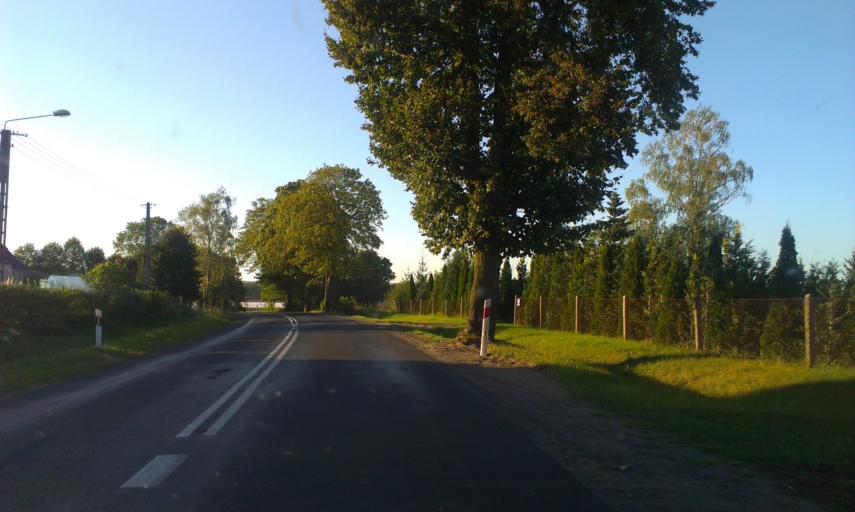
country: PL
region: Pomeranian Voivodeship
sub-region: Powiat czluchowski
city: Rzeczenica
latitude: 53.6528
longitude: 17.1419
